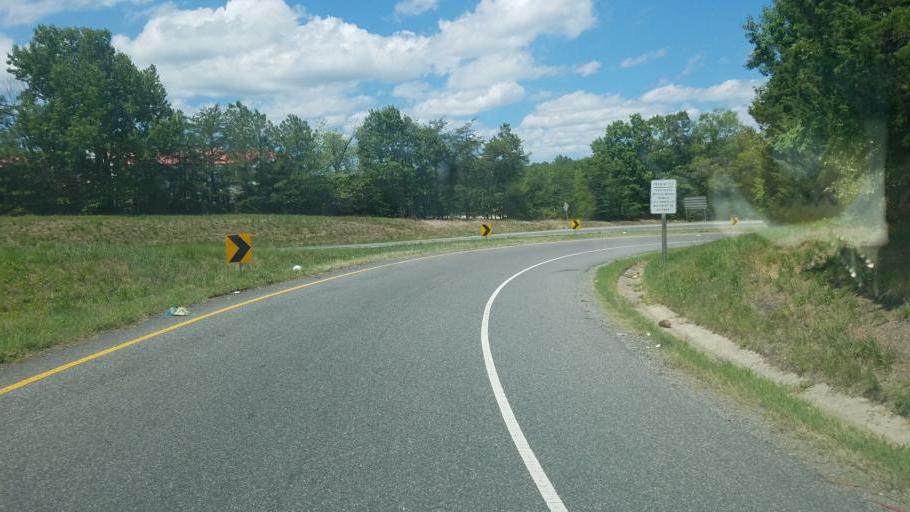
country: US
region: Virginia
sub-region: Caroline County
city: Bowling Green
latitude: 37.9356
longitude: -77.4725
